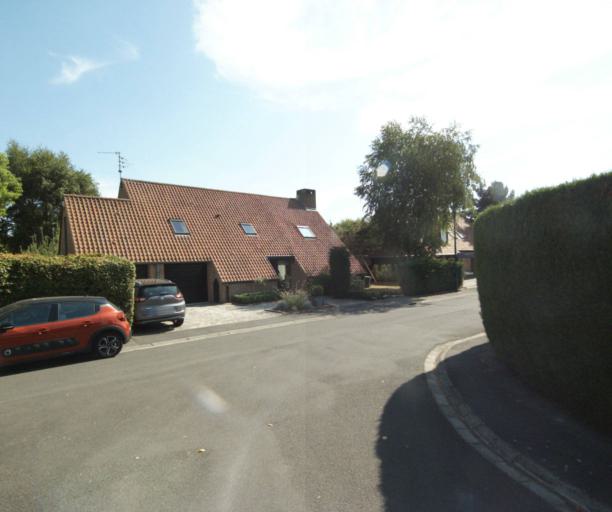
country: FR
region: Nord-Pas-de-Calais
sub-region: Departement du Nord
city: Bondues
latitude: 50.7092
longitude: 3.0738
